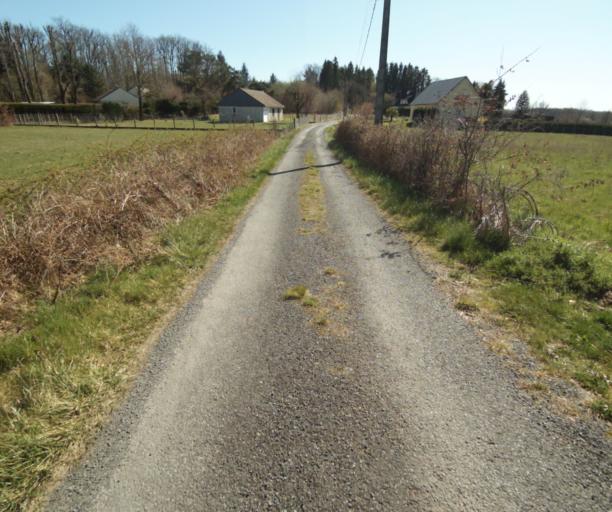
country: FR
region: Limousin
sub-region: Departement de la Correze
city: Chamboulive
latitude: 45.4574
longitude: 1.7275
